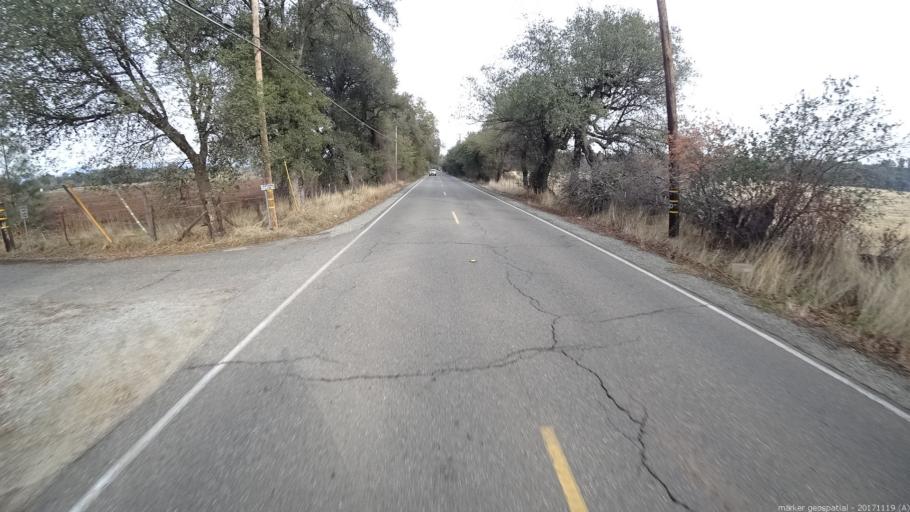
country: US
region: California
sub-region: Shasta County
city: Redding
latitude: 40.5275
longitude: -122.3337
